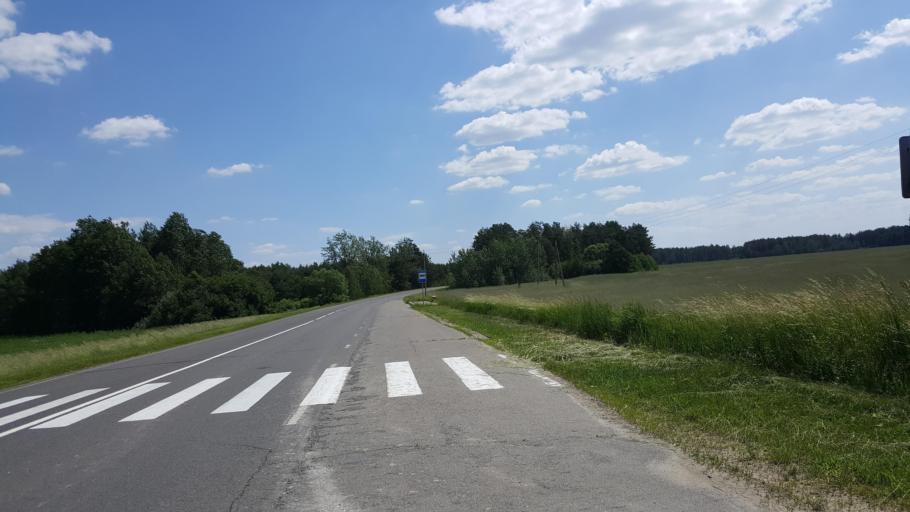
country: BY
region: Brest
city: Zhabinka
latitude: 52.2052
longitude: 24.0904
